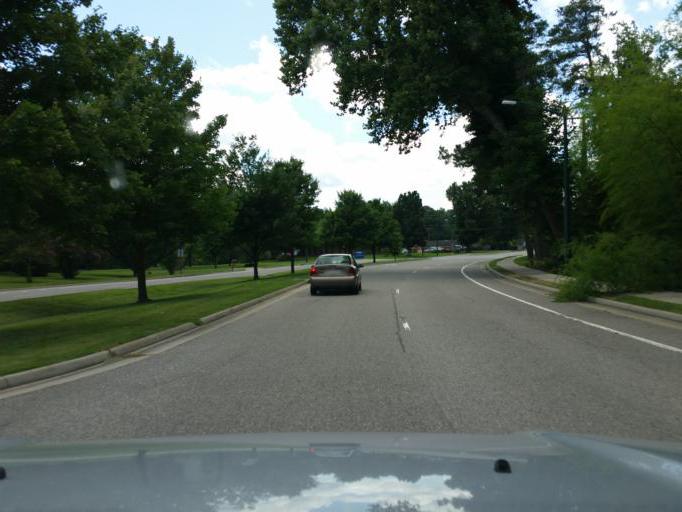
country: US
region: Virginia
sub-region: City of Williamsburg
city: Williamsburg
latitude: 37.2878
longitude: -76.6864
